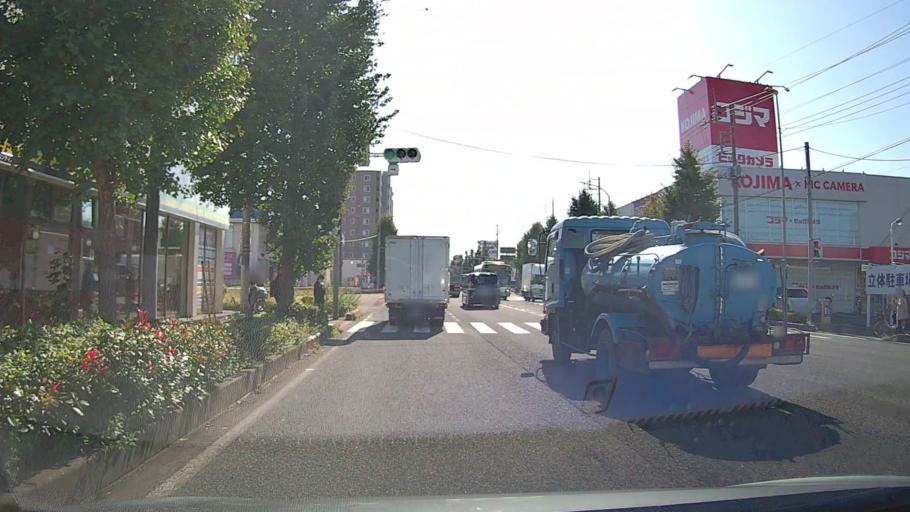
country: JP
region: Saitama
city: Wako
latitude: 35.7679
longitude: 139.6200
